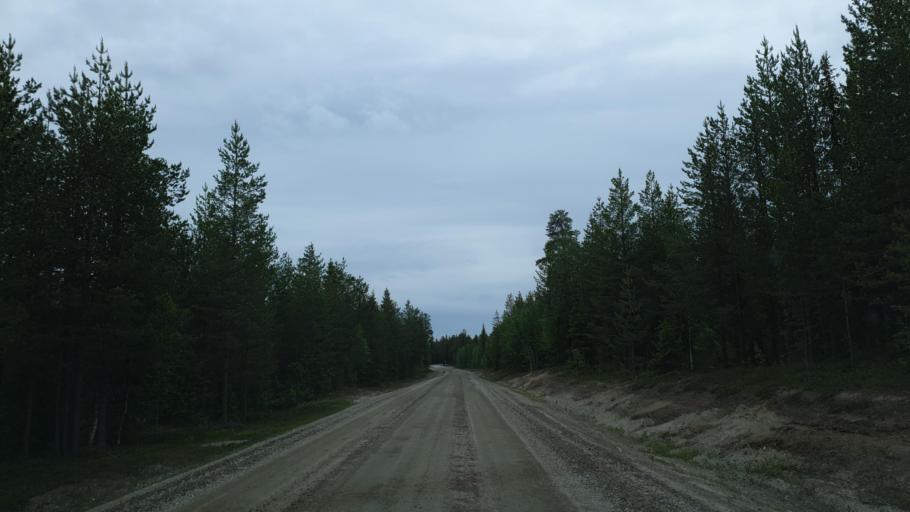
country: SE
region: Vaesterbotten
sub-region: Sorsele Kommun
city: Sorsele
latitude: 65.5554
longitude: 17.5055
